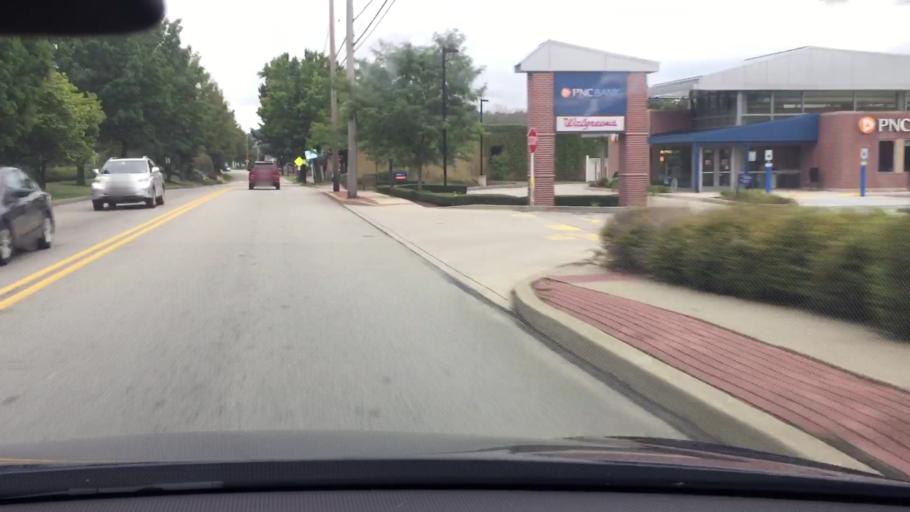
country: US
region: Pennsylvania
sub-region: Allegheny County
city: Oakmont
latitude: 40.5251
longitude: -79.8413
